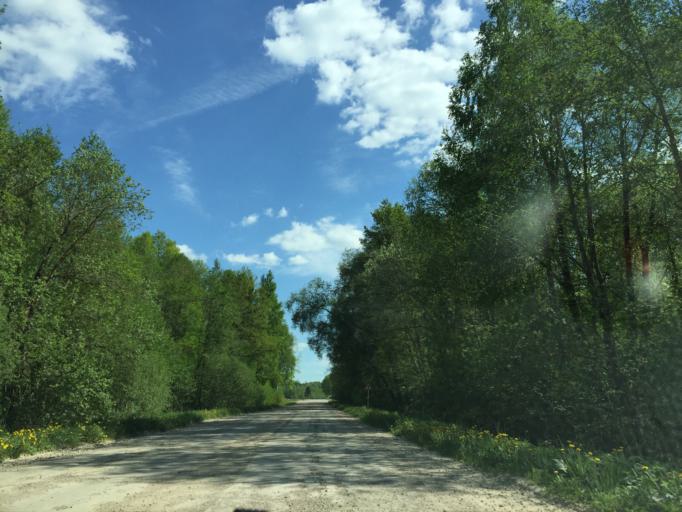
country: LV
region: Rundales
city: Pilsrundale
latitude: 56.4253
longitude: 24.0444
